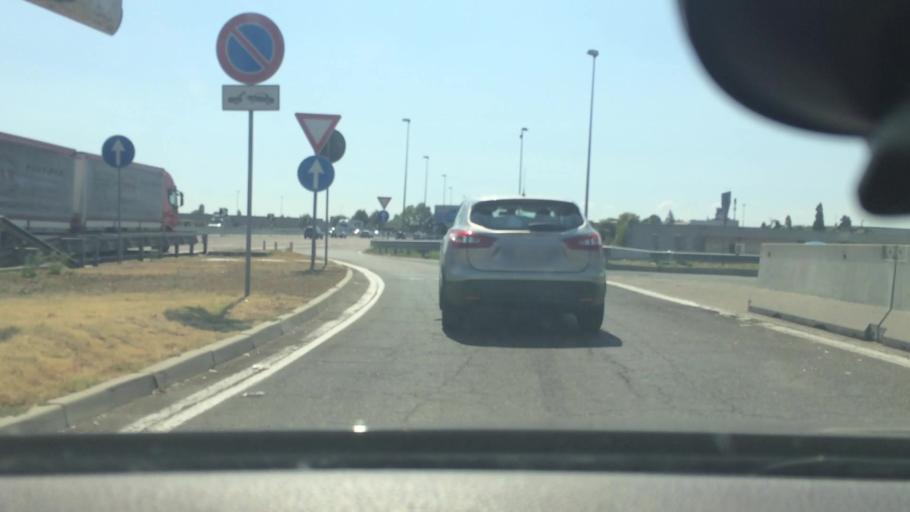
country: IT
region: Emilia-Romagna
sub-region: Provincia di Modena
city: Campogalliano
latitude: 44.6616
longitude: 10.8570
